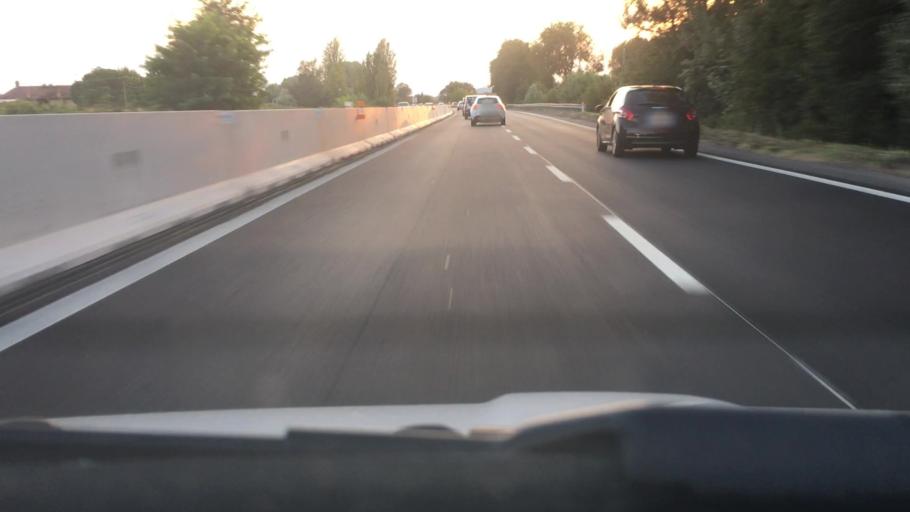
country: IT
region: Emilia-Romagna
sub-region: Provincia di Ferrara
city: Gaibanella-Sant'Edigio
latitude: 44.7986
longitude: 11.6575
